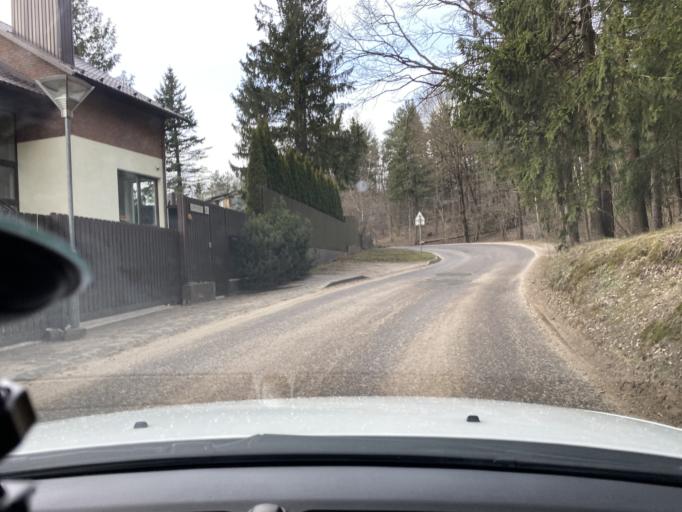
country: LT
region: Vilnius County
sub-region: Vilnius
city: Fabijoniskes
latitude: 54.7584
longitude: 25.2554
